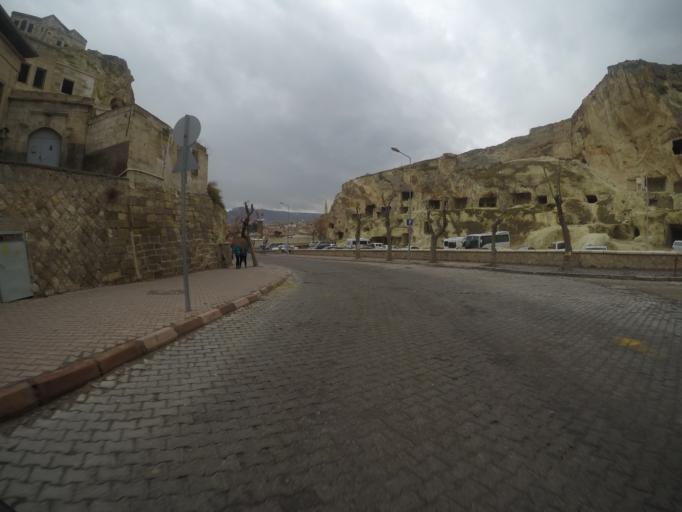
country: TR
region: Nevsehir
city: Urgub
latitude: 38.6314
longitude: 34.9093
